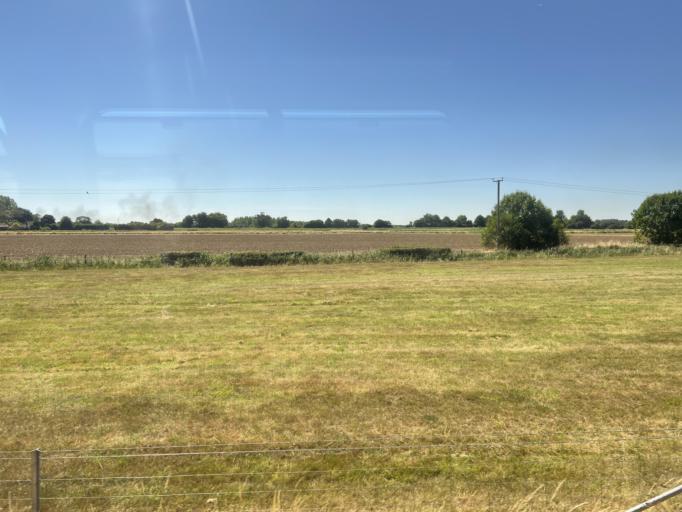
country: GB
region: England
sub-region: Lincolnshire
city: Wainfleet All Saints
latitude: 53.1110
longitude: 0.2219
